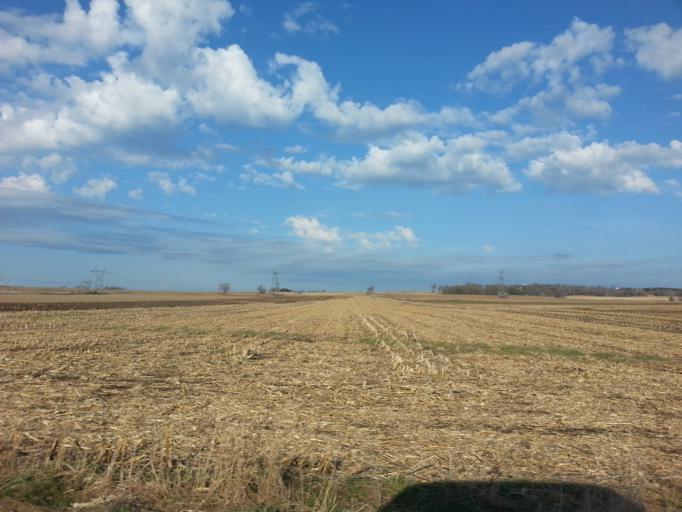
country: US
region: Minnesota
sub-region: Washington County
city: Afton
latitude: 44.8584
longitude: -92.8422
